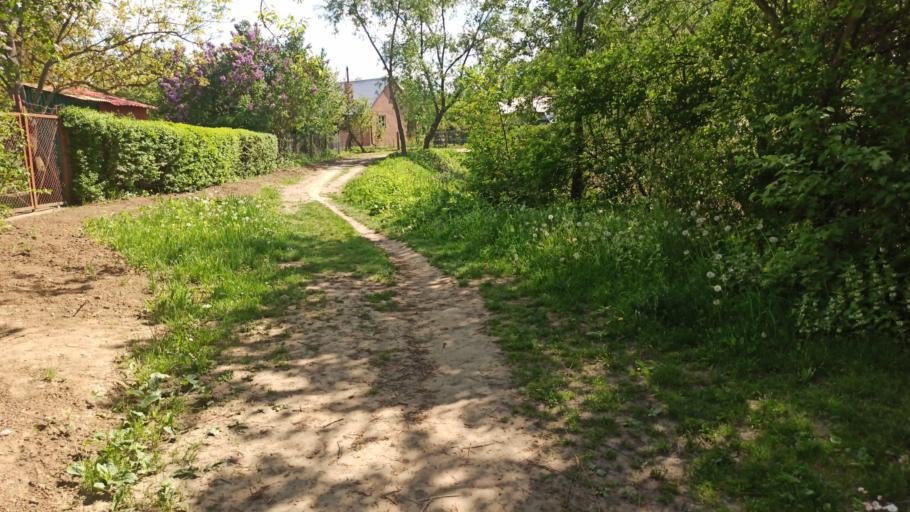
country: PL
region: Subcarpathian Voivodeship
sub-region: Powiat jaroslawski
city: Radymno
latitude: 49.9532
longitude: 22.8334
